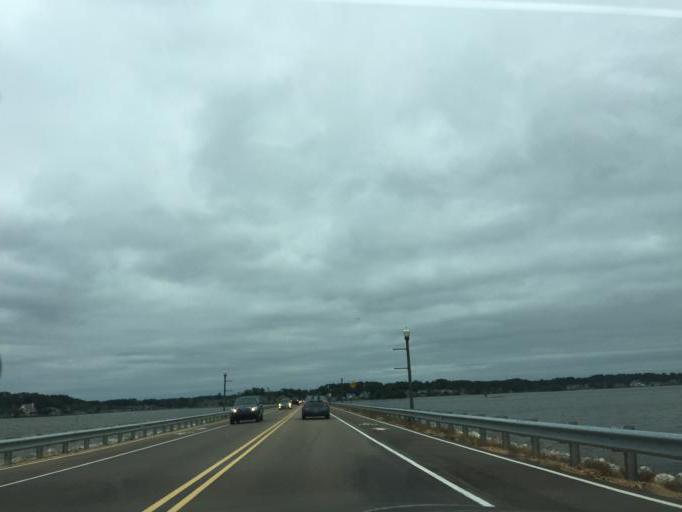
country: US
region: Mississippi
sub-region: Madison County
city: Madison
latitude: 32.3994
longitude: -90.0219
